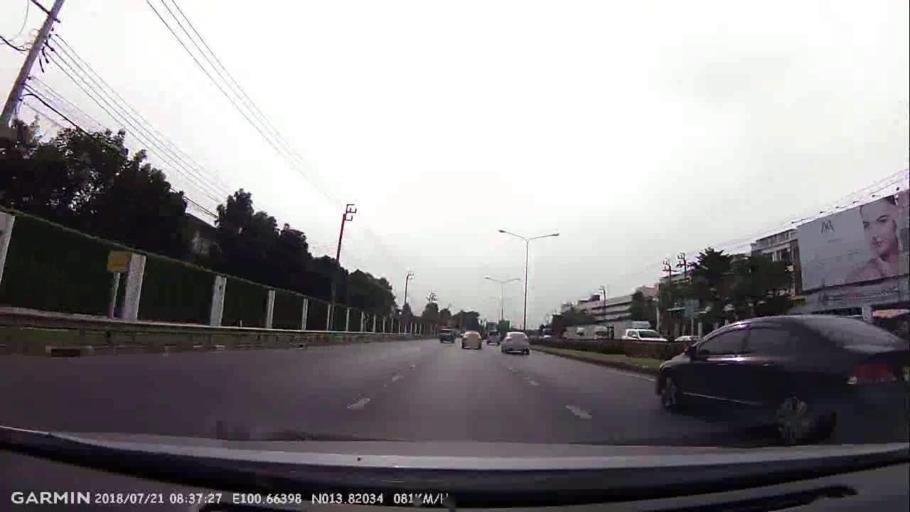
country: TH
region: Bangkok
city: Khan Na Yao
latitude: 13.8204
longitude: 100.6642
